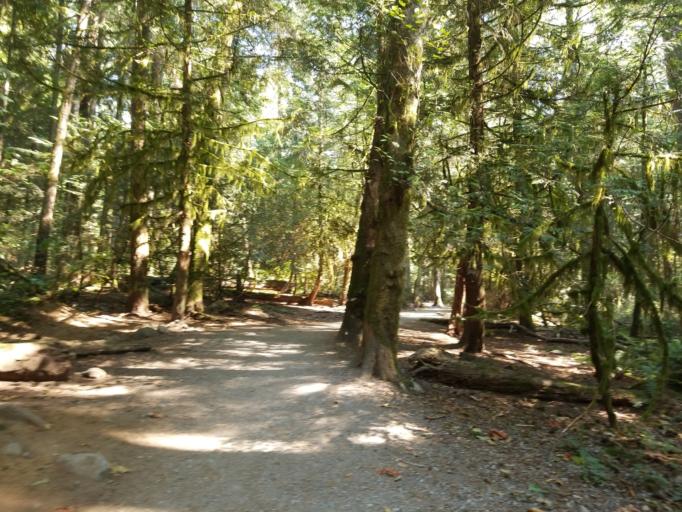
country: CA
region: British Columbia
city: West End
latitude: 49.2515
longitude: -123.2112
